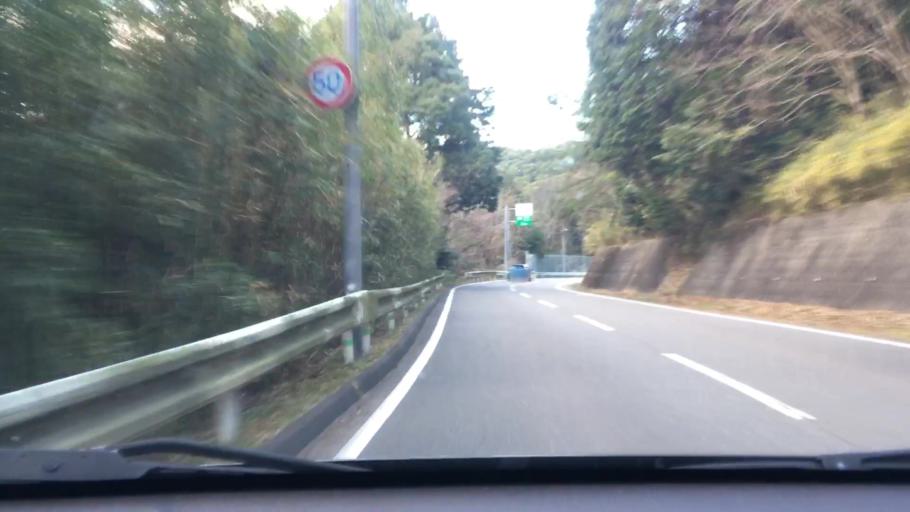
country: JP
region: Oita
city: Hiji
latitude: 33.3658
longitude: 131.4671
